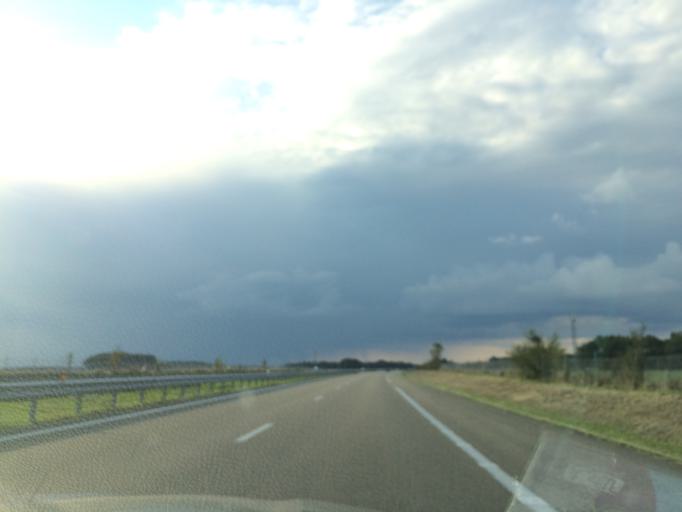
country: FR
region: Ile-de-France
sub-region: Departement de Seine-et-Marne
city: Egreville
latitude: 48.1336
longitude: 2.9331
